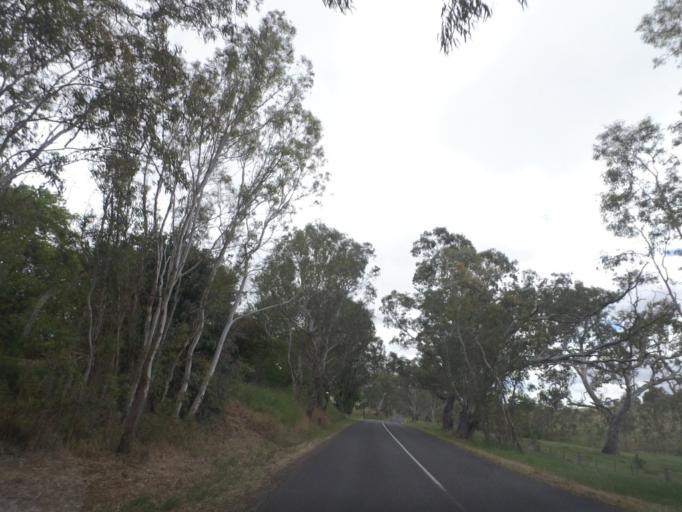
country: AU
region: Victoria
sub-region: Whittlesea
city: Whittlesea
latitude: -37.1956
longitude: 145.0381
